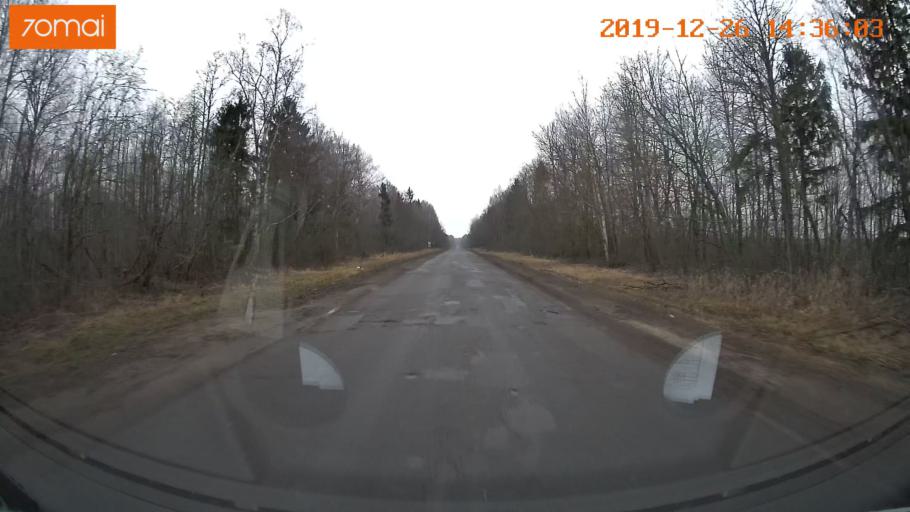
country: RU
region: Jaroslavl
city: Poshekhon'ye
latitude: 58.4152
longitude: 38.9777
